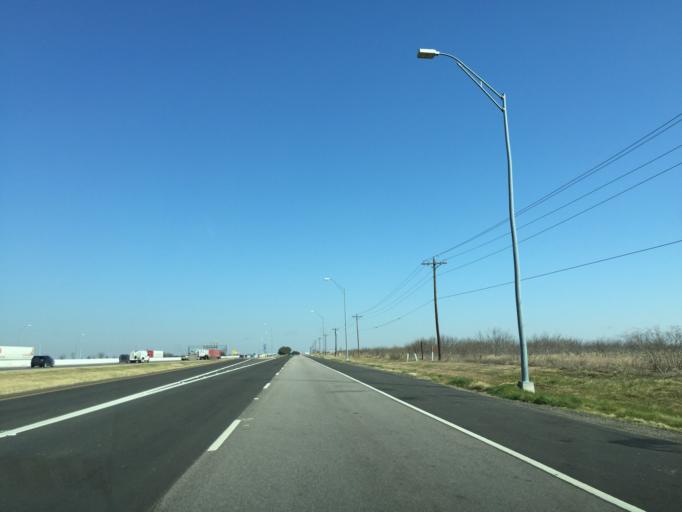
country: US
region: Texas
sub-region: Williamson County
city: Serenada
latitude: 30.7135
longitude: -97.6471
